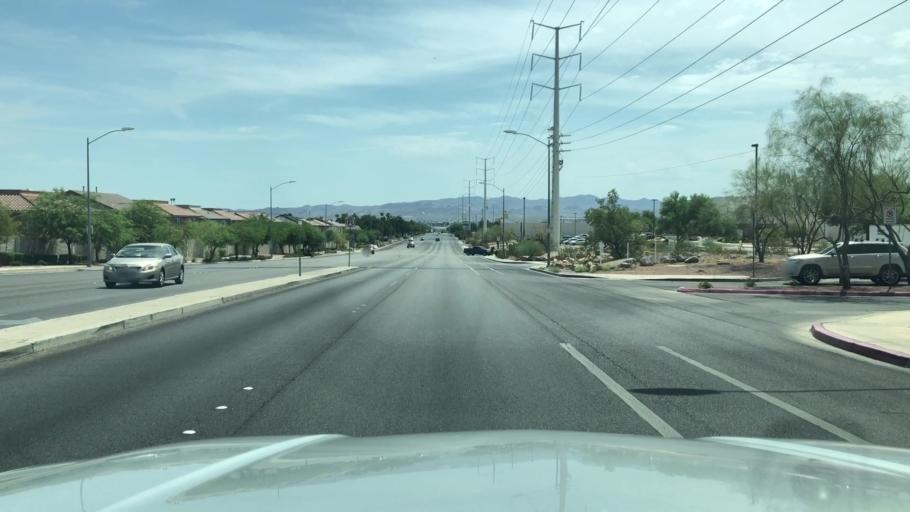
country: US
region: Nevada
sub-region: Clark County
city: Whitney
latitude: 36.0417
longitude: -115.0460
